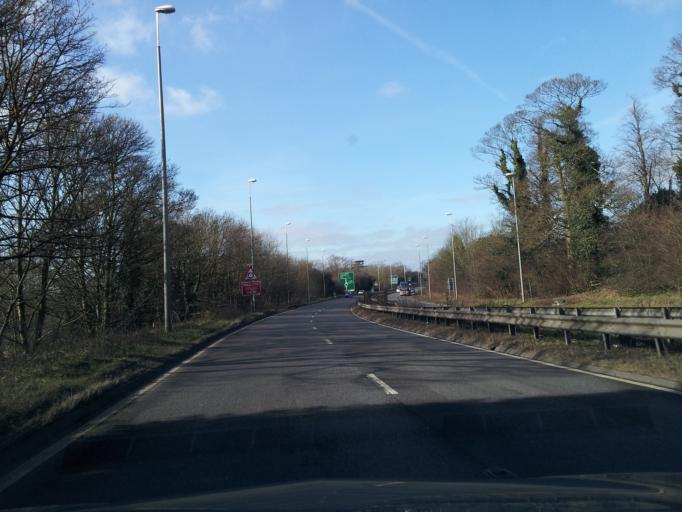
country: GB
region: England
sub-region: Nottinghamshire
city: Ruddington
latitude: 52.9055
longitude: -1.1382
